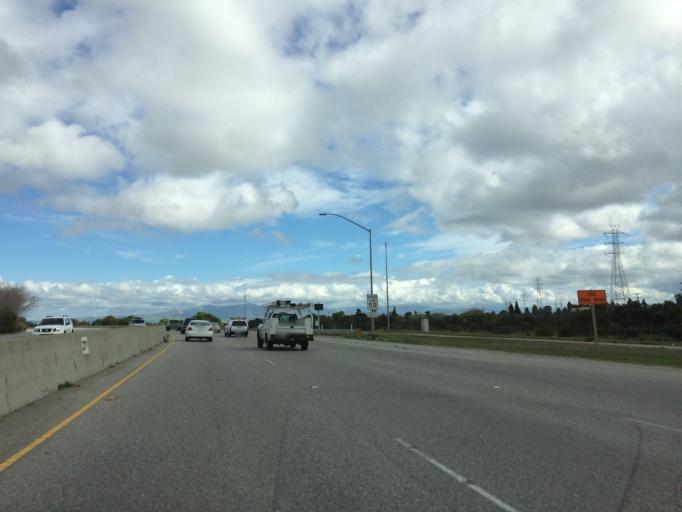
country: US
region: California
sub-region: San Mateo County
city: East Palo Alto
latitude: 37.4820
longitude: -122.1499
